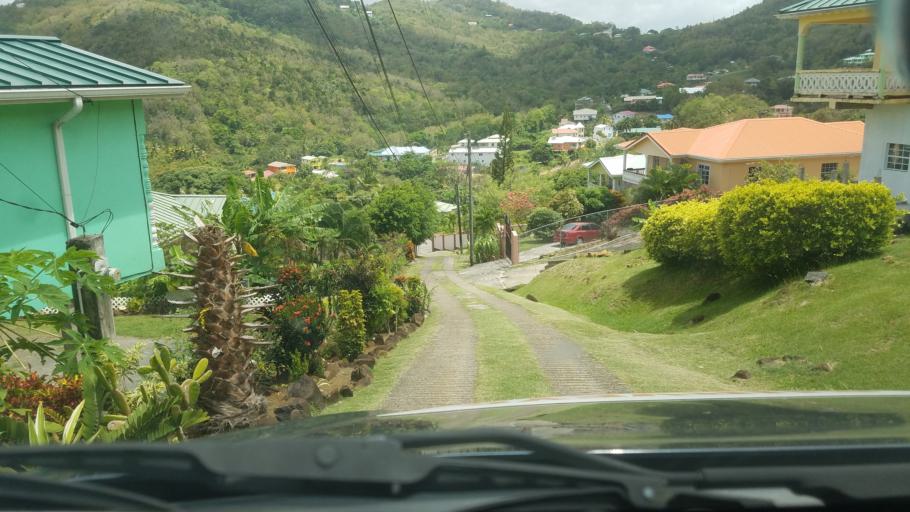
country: LC
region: Gros-Islet
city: Gros Islet
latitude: 14.0620
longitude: -60.9488
